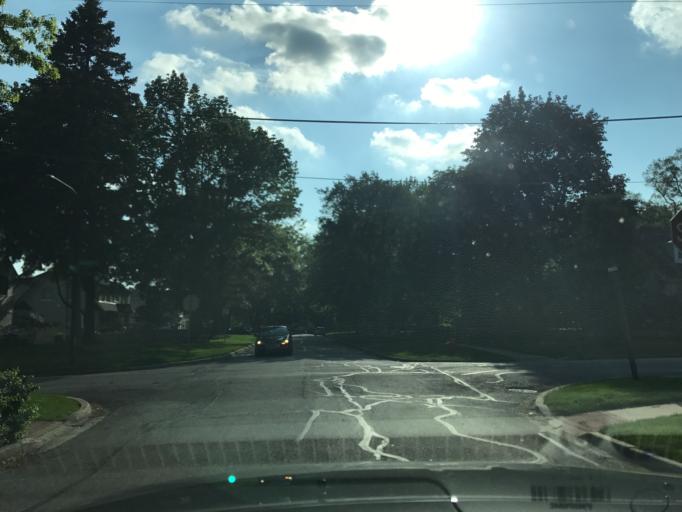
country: US
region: Illinois
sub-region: DuPage County
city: Naperville
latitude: 41.7715
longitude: -88.1404
